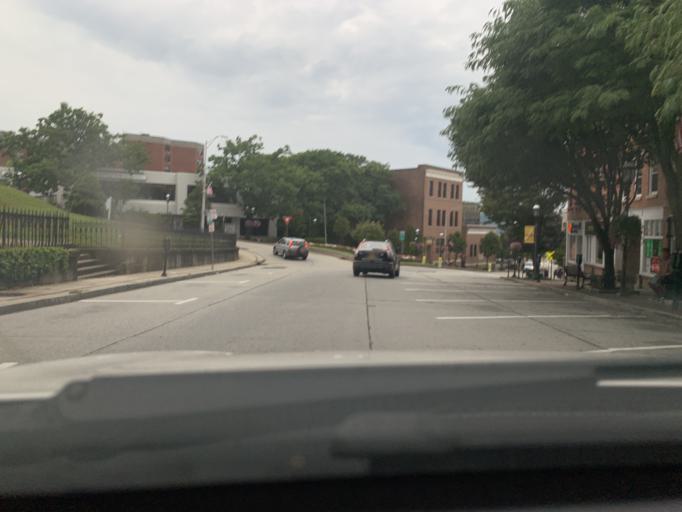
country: US
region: New York
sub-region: Westchester County
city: Ossining
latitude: 41.1616
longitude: -73.8619
